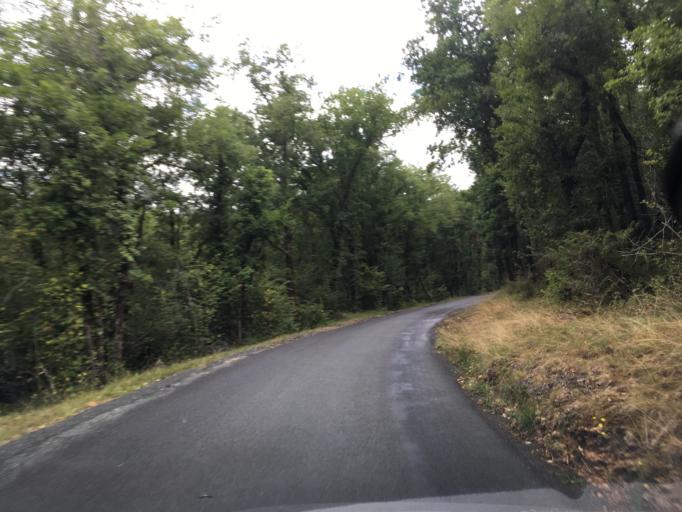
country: FR
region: Aquitaine
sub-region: Departement de la Dordogne
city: Saint-Cyprien
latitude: 44.9484
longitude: 1.0472
